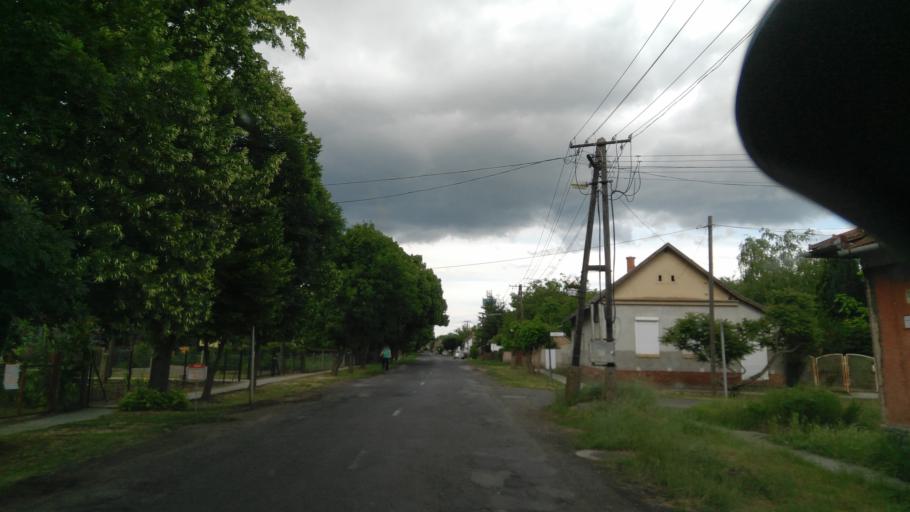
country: HU
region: Bekes
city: Gadoros
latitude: 46.6679
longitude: 20.5919
